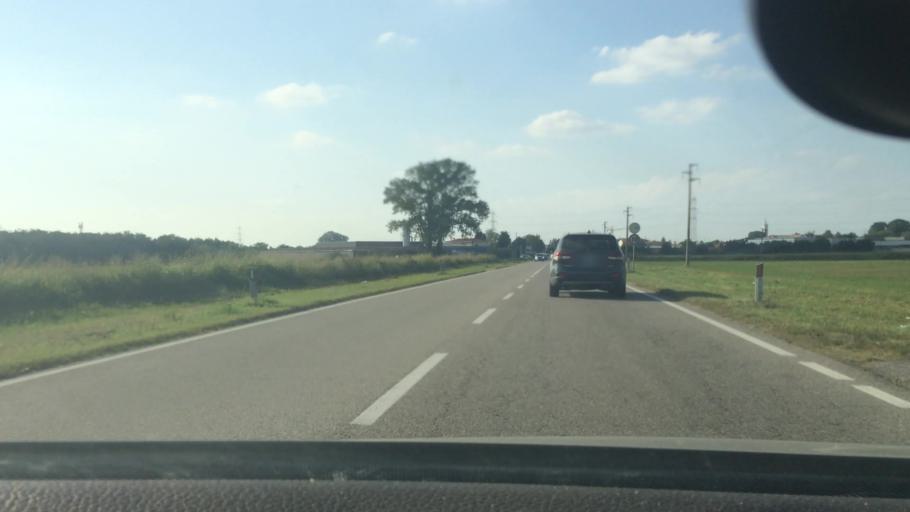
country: IT
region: Lombardy
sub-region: Citta metropolitana di Milano
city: Buscate
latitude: 45.5354
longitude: 8.8244
